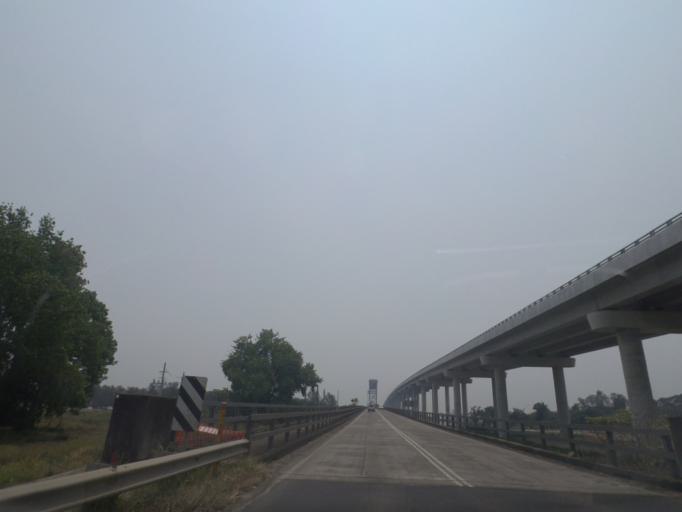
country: AU
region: New South Wales
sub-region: Clarence Valley
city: Maclean
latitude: -29.4346
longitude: 153.2406
